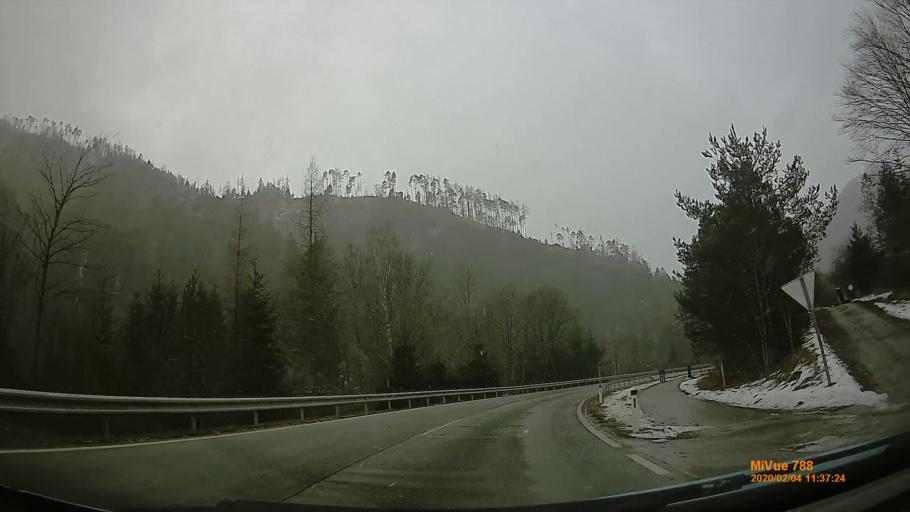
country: AT
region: Styria
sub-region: Politischer Bezirk Bruck-Muerzzuschlag
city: Neuberg an der Muerz
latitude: 47.6712
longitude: 15.5398
